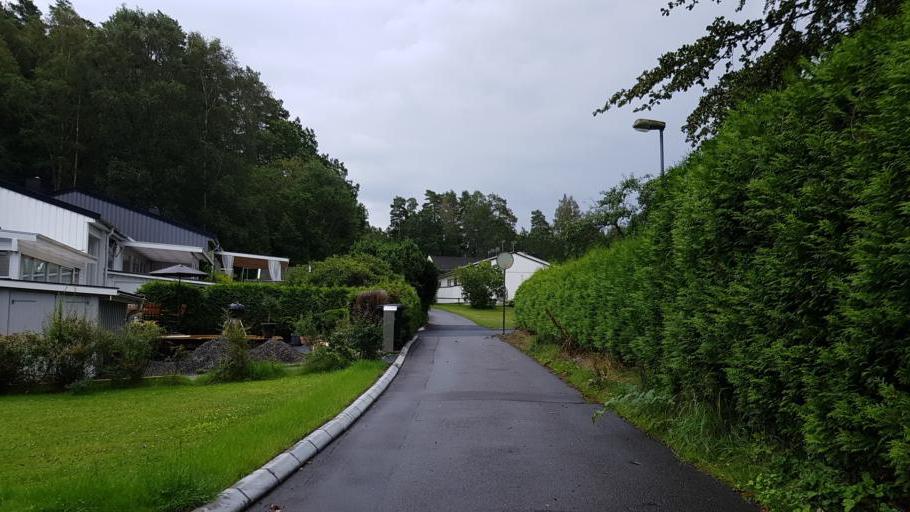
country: SE
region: Vaestra Goetaland
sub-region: Harryda Kommun
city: Molnlycke
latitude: 57.6523
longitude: 12.1113
